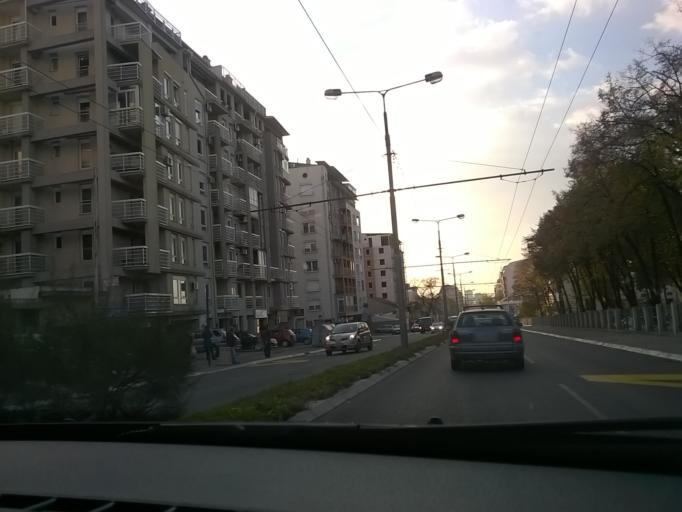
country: RS
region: Central Serbia
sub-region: Belgrade
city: Palilula
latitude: 44.8000
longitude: 20.4993
